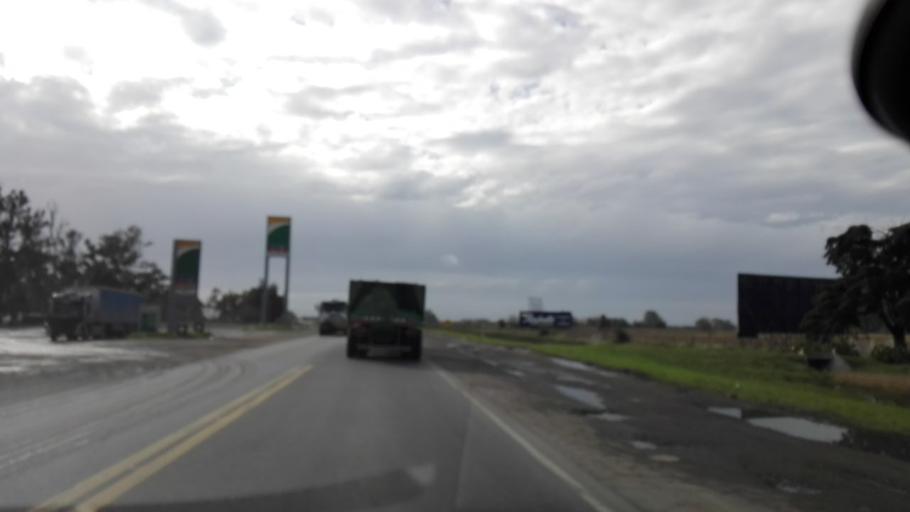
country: AR
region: Buenos Aires
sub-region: Partido de Las Flores
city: Las Flores
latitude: -36.0154
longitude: -59.0695
